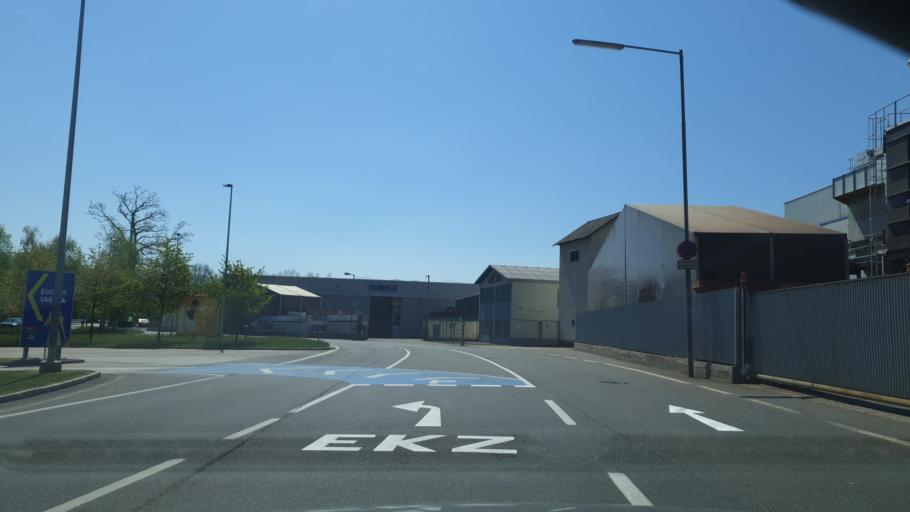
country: AT
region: Upper Austria
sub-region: Politischer Bezirk Vocklabruck
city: Vocklabruck
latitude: 48.0030
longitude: 13.6671
